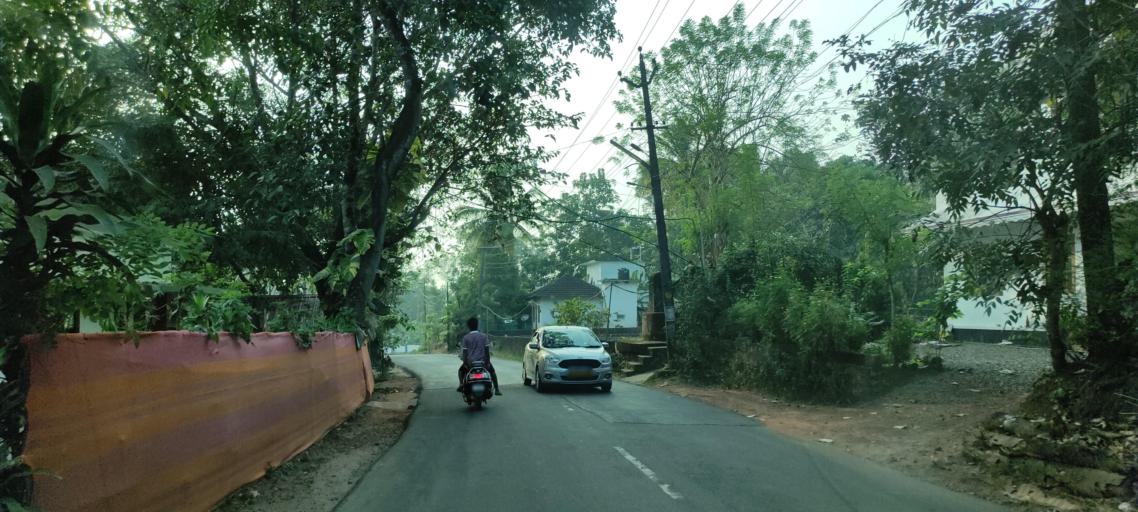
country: IN
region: Kerala
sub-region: Kottayam
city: Vaikam
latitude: 9.6927
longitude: 76.4653
